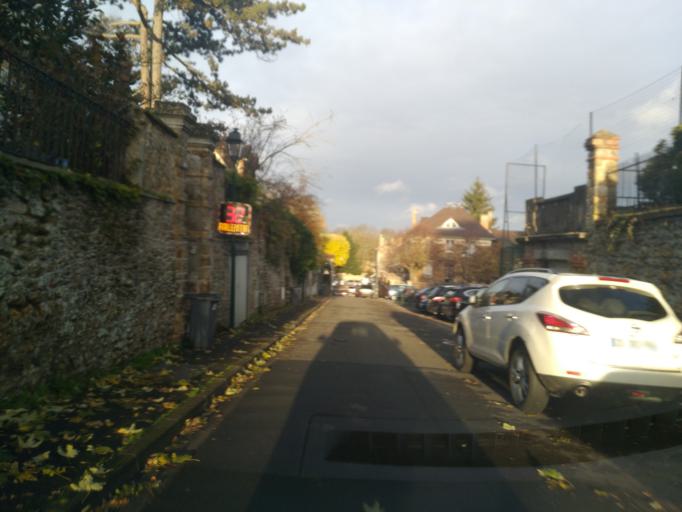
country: FR
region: Ile-de-France
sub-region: Departement des Yvelines
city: Fourqueux
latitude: 48.8855
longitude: 2.0645
